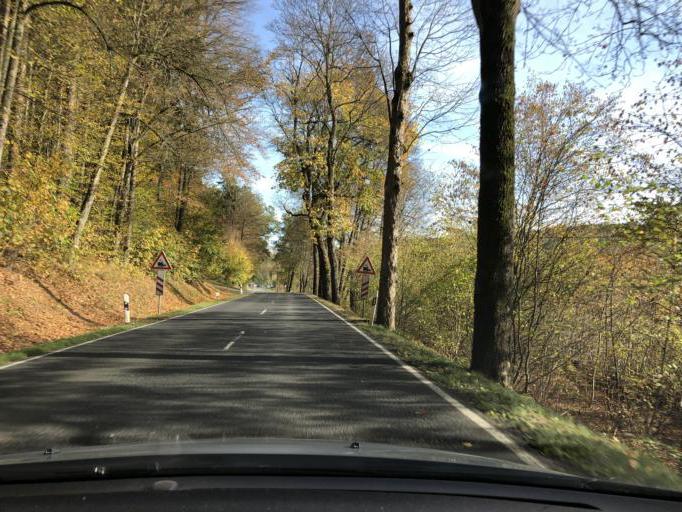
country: DE
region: Thuringia
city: Ehrenberg
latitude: 50.4877
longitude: 10.6858
